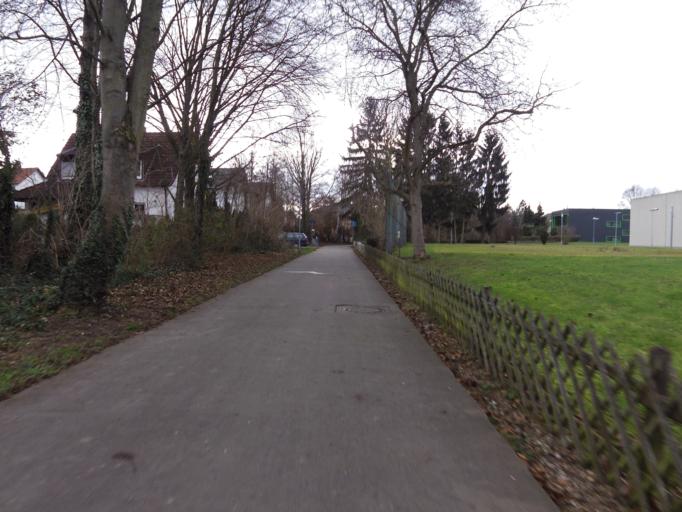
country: DE
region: Rheinland-Pfalz
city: Frankenthal
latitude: 49.5403
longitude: 8.3763
